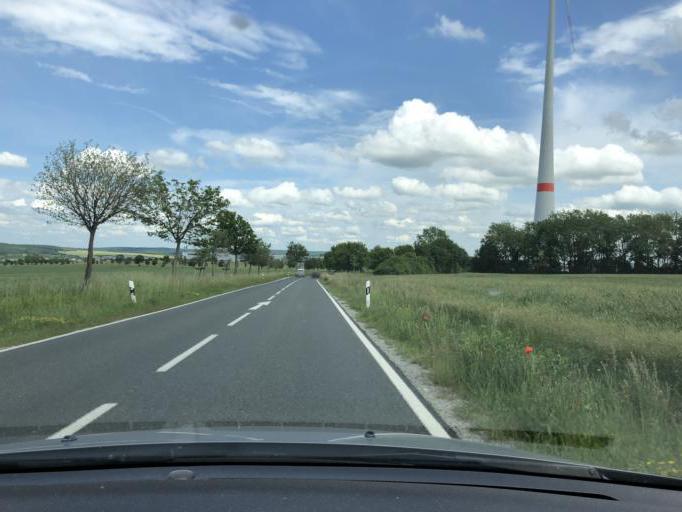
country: DE
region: Thuringia
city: Kullstedt
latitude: 51.2995
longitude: 10.2775
